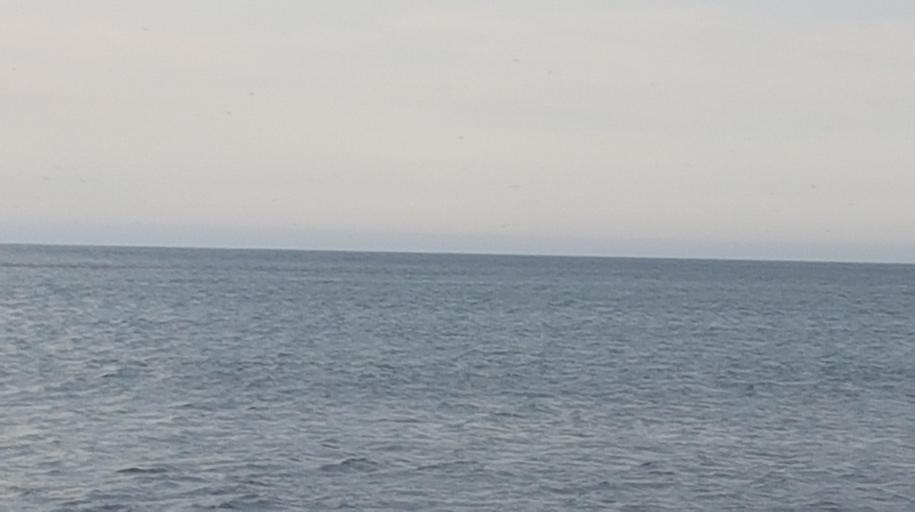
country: PE
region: Ancash
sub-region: Provincia de Santa
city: Puerto Santa
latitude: -8.9853
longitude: -78.6461
